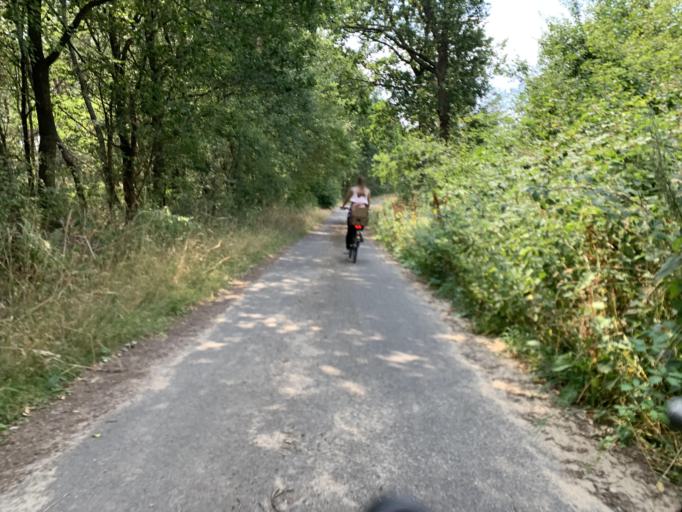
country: DE
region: Lower Saxony
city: Thomasburg
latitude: 53.1986
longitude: 10.6516
